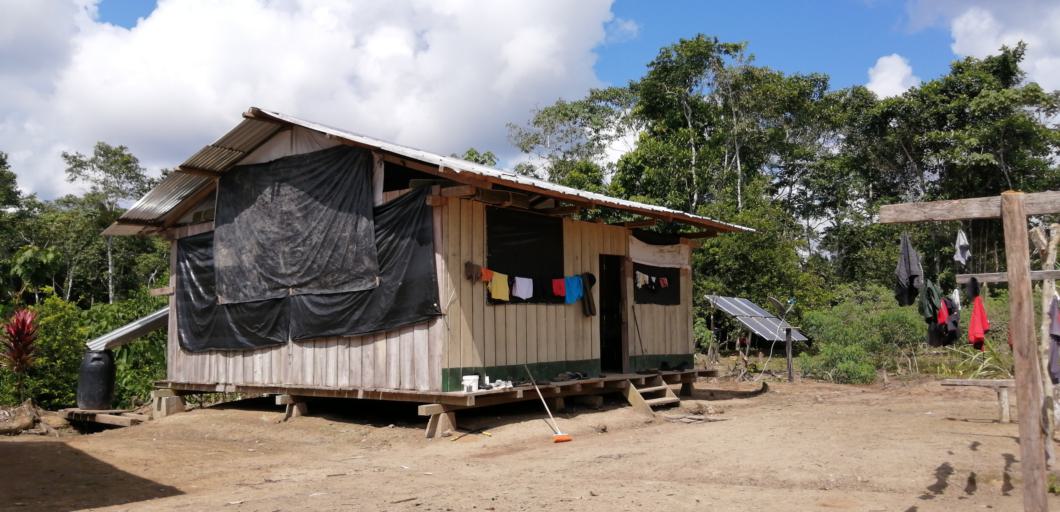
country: EC
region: Morona-Santiago
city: Taisha
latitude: -2.8089
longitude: -77.3022
